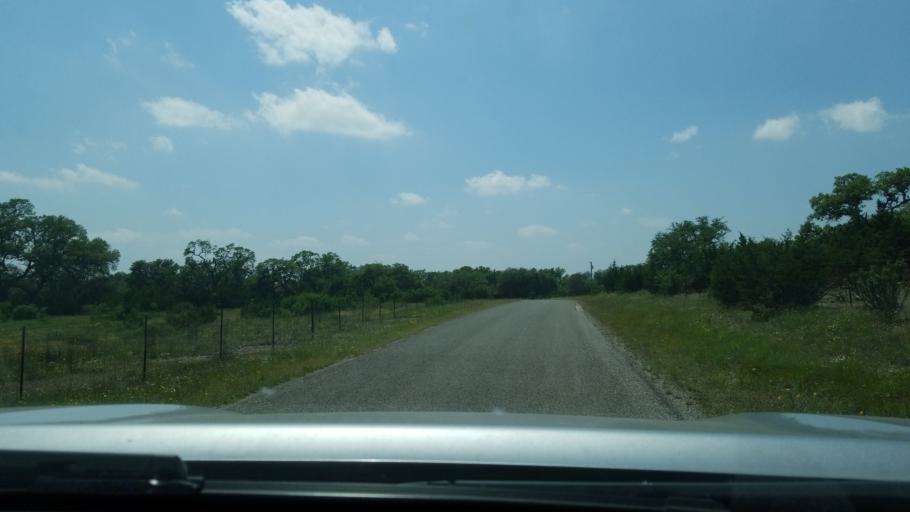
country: US
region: Texas
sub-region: Blanco County
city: Blanco
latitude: 29.9869
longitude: -98.5427
